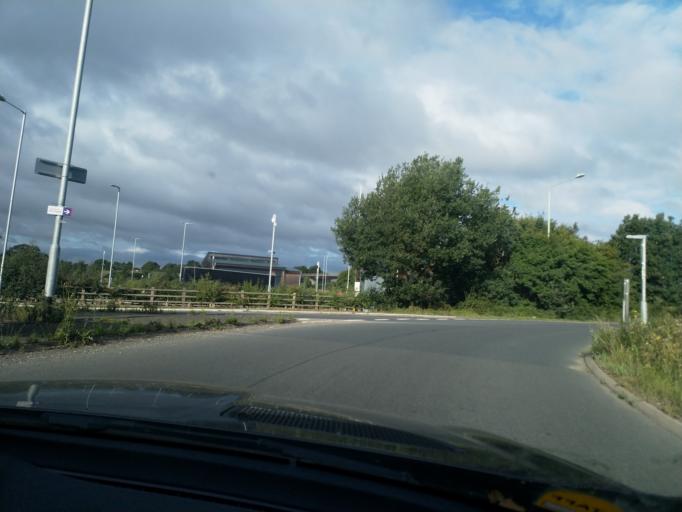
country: GB
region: England
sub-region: Suffolk
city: Woolpit
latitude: 52.2325
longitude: 0.8953
